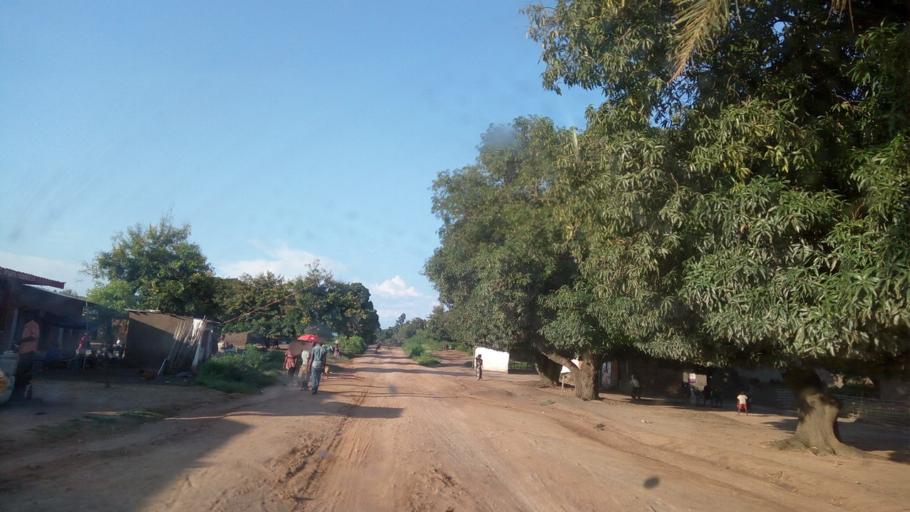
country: BI
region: Bururi
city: Rumonge
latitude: -4.1888
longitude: 29.0526
